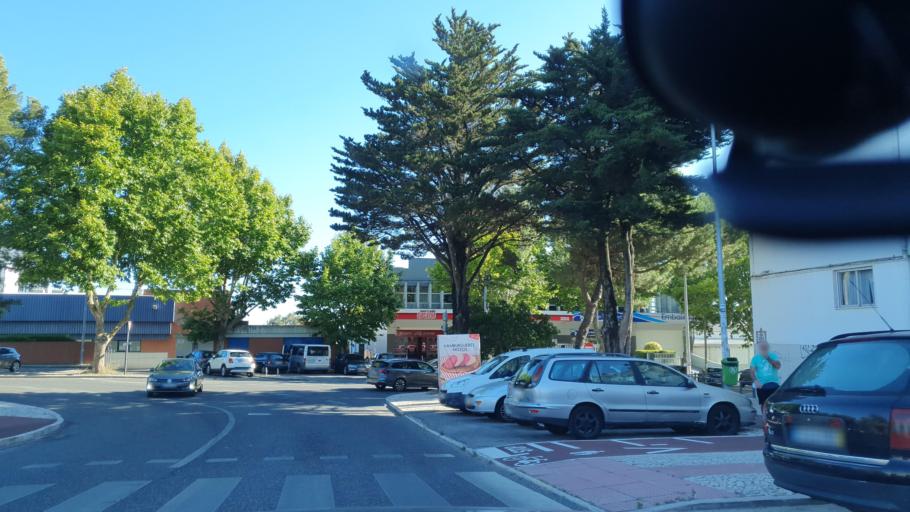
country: PT
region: Lisbon
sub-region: Oeiras
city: Barcarena
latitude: 38.7497
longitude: -9.2768
